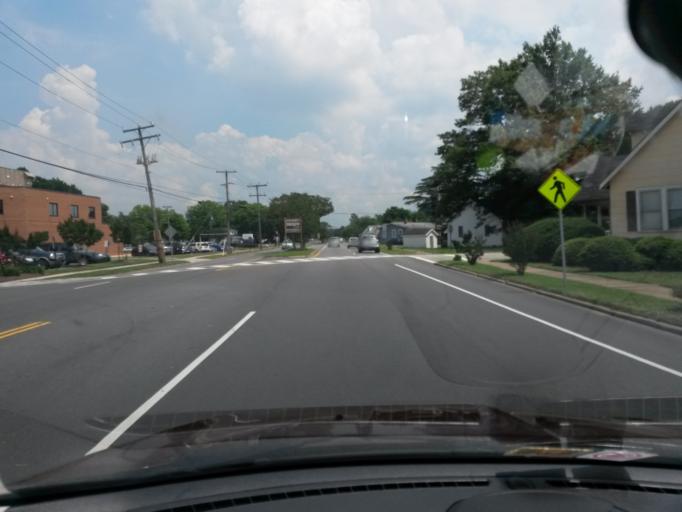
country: US
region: Virginia
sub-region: City of Hopewell
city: Hopewell
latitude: 37.3077
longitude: -77.2925
